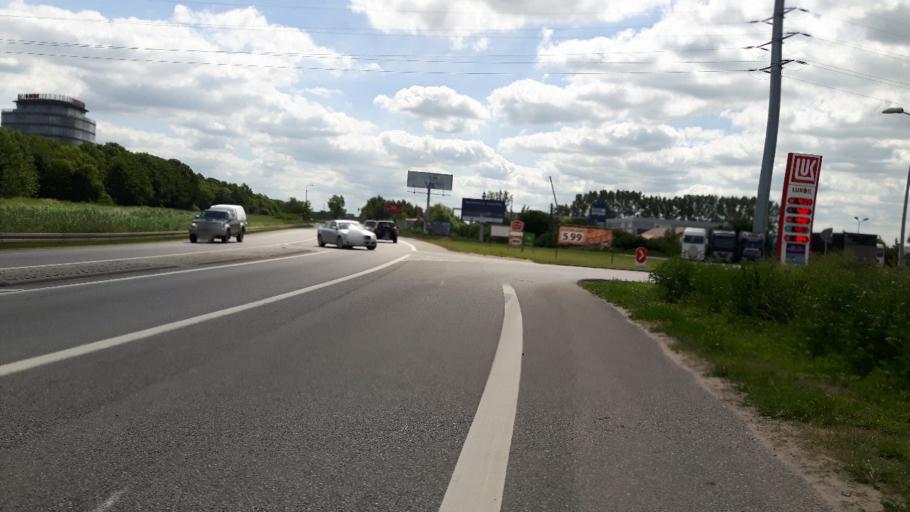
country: PL
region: Pomeranian Voivodeship
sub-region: Gdansk
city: Gdansk
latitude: 54.3451
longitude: 18.7193
